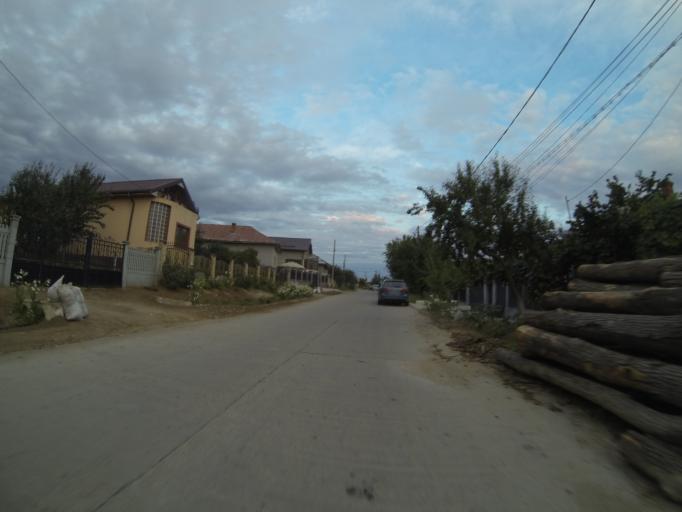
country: RO
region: Dolj
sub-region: Comuna Isalnita
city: Isalnita
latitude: 44.4172
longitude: 23.7264
